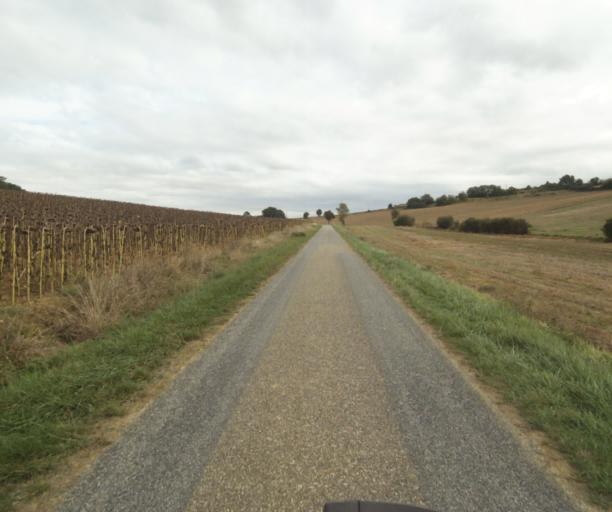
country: FR
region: Midi-Pyrenees
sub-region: Departement du Tarn-et-Garonne
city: Beaumont-de-Lomagne
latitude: 43.8272
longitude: 1.0738
